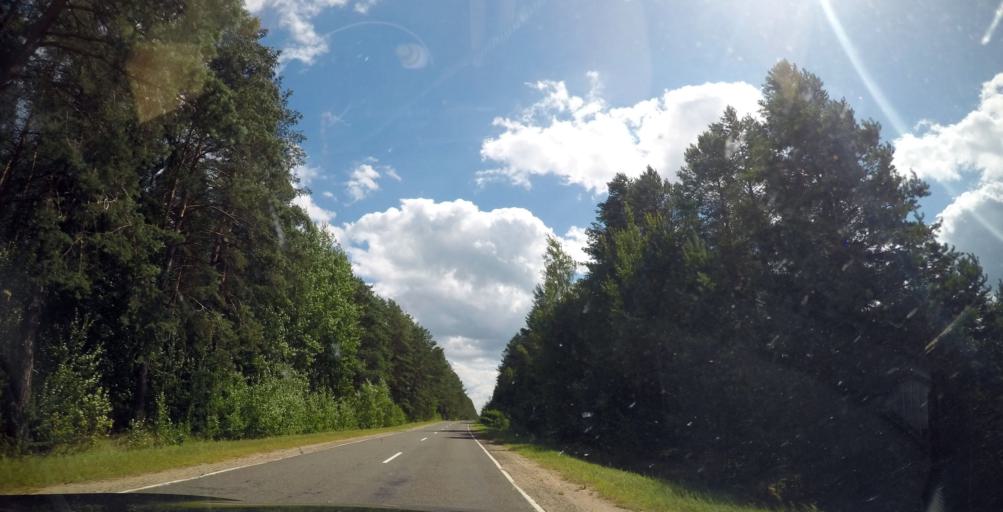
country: LT
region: Alytaus apskritis
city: Druskininkai
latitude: 53.8694
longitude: 24.1630
